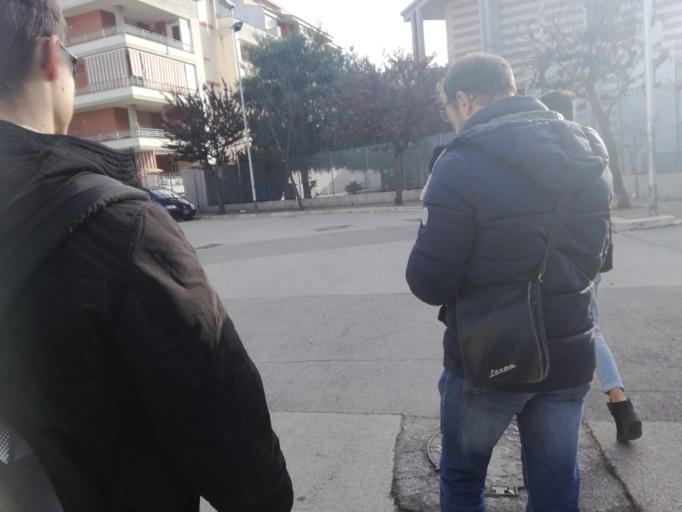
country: IT
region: Apulia
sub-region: Provincia di Barletta - Andria - Trani
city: Andria
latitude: 41.2381
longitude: 16.2963
